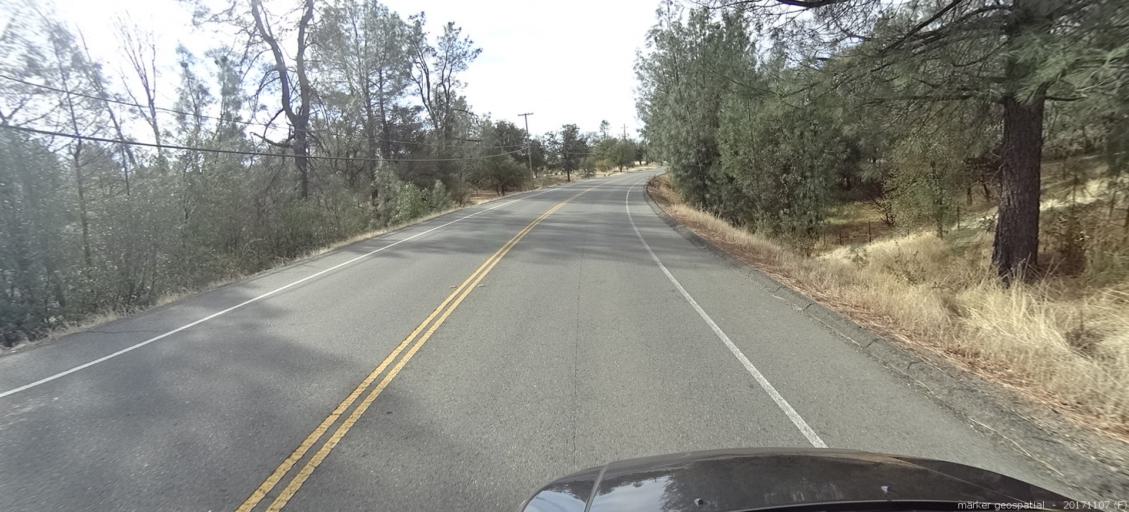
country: US
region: California
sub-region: Shasta County
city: Shasta
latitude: 40.5239
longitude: -122.4763
